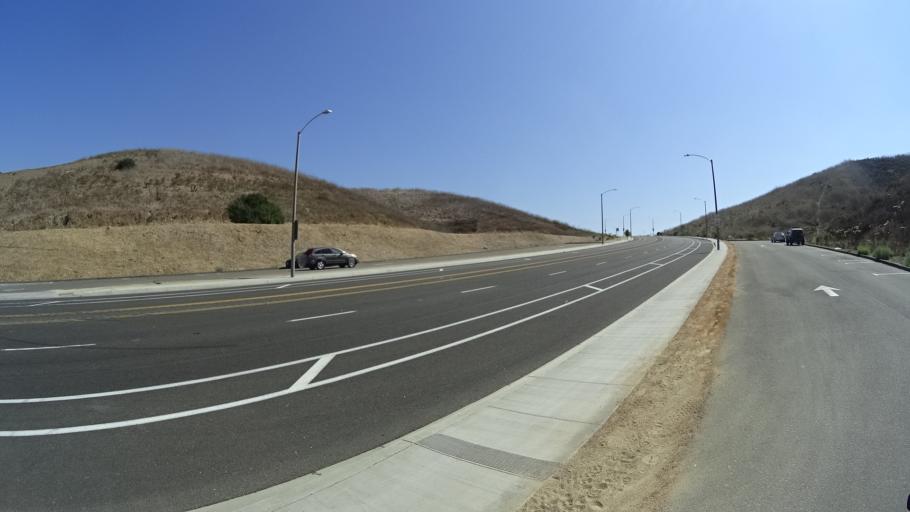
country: US
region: California
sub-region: Orange County
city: San Clemente
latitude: 33.4721
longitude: -117.6136
